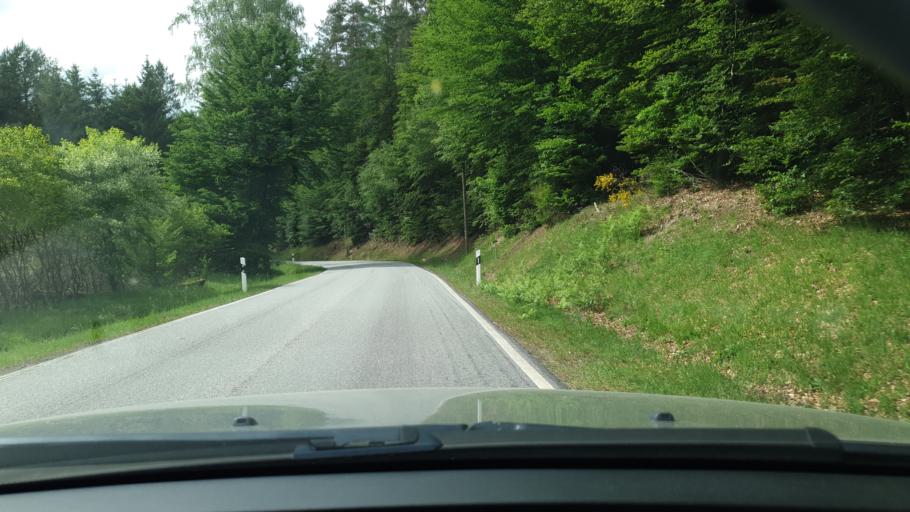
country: DE
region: Rheinland-Pfalz
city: Trippstadt
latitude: 49.3928
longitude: 7.7843
